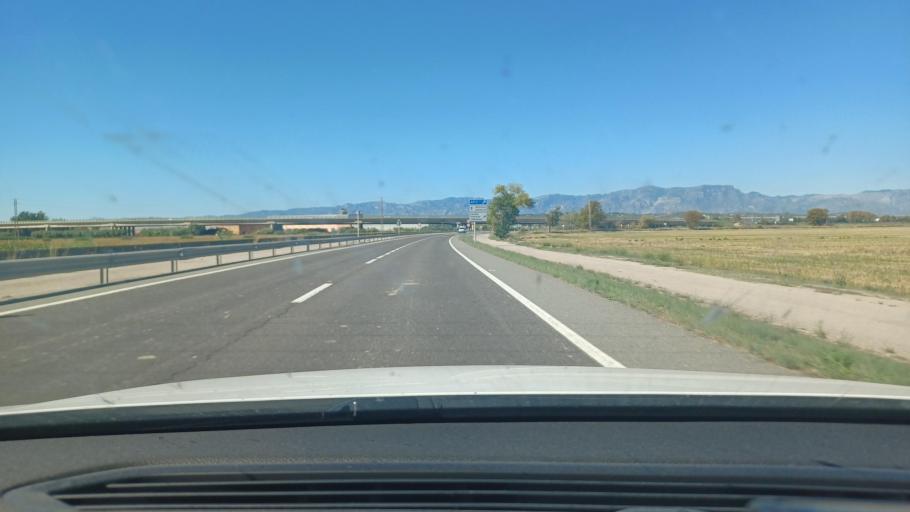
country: ES
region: Catalonia
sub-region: Provincia de Tarragona
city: Amposta
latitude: 40.7135
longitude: 0.5982
